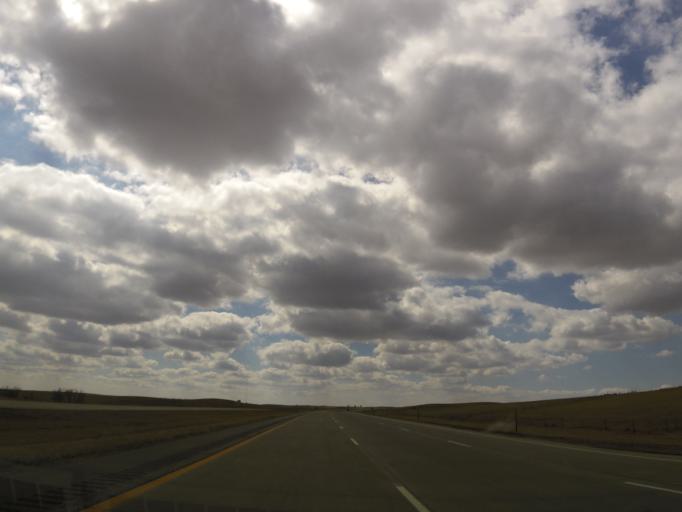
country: US
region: South Dakota
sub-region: Roberts County
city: Sisseton
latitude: 45.3993
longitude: -97.0242
